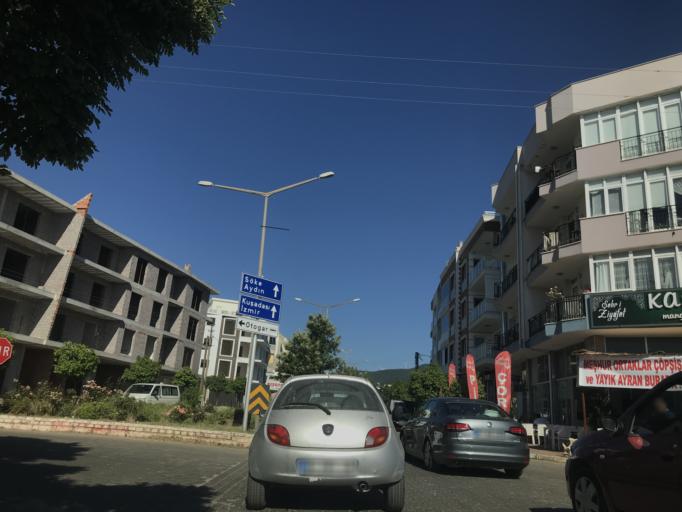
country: TR
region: Aydin
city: Davutlar
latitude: 37.7335
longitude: 27.2844
